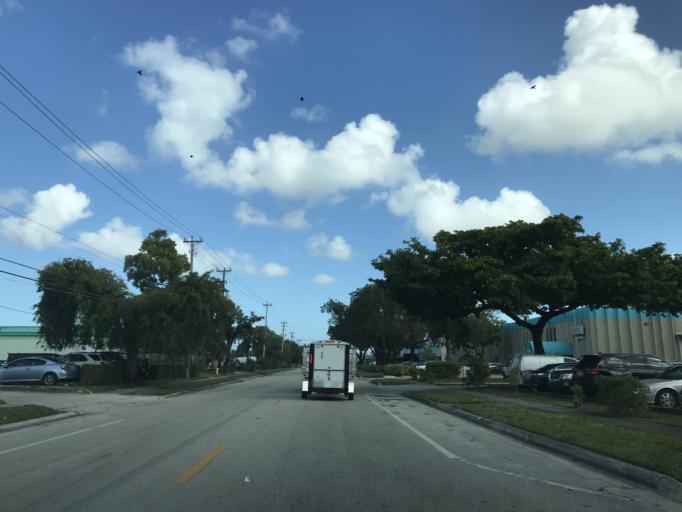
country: US
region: Florida
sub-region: Broward County
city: Margate
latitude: 26.2486
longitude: -80.1972
